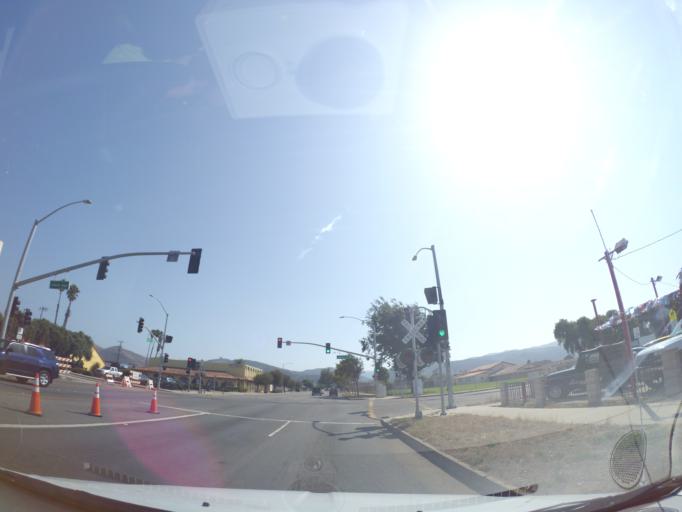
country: US
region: California
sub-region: Santa Barbara County
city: Lompoc
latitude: 34.6442
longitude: -120.4579
